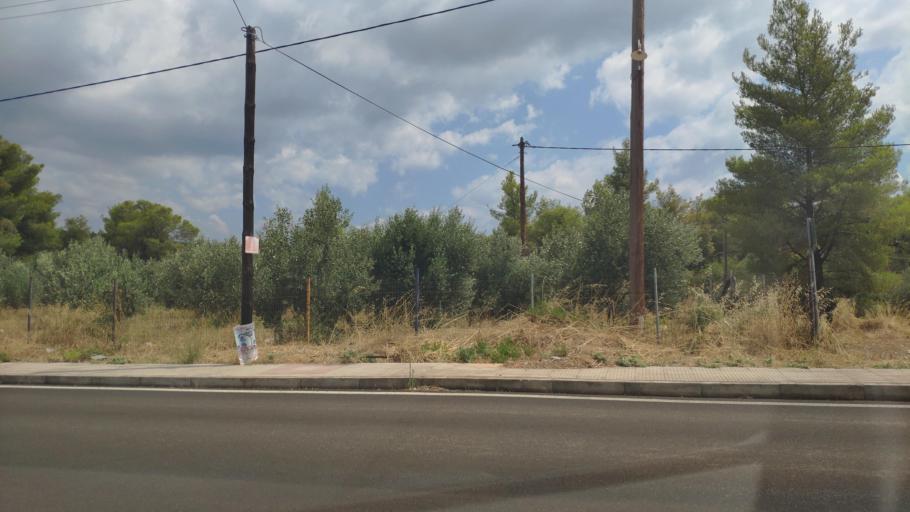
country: GR
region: Central Greece
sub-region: Nomos Fthiotidos
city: Malesina
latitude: 38.6465
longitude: 23.1996
